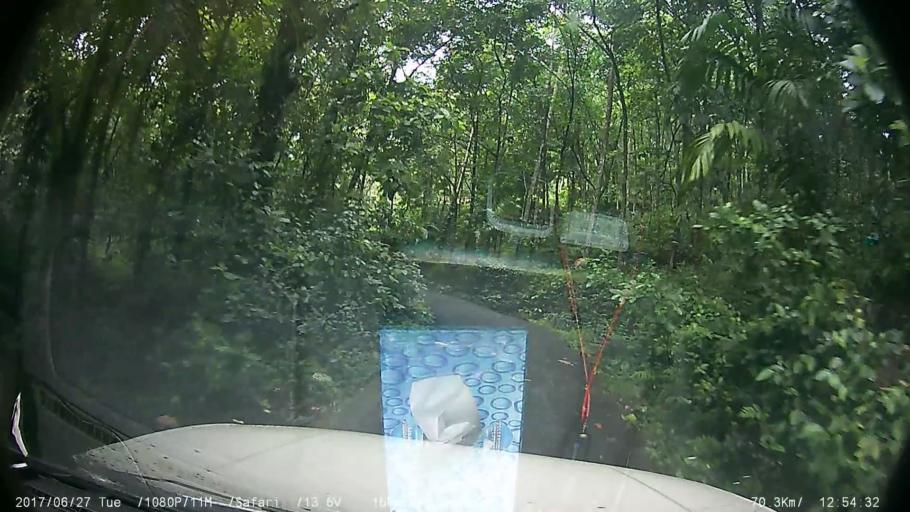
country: IN
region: Kerala
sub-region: Kottayam
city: Palackattumala
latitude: 9.7797
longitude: 76.5447
